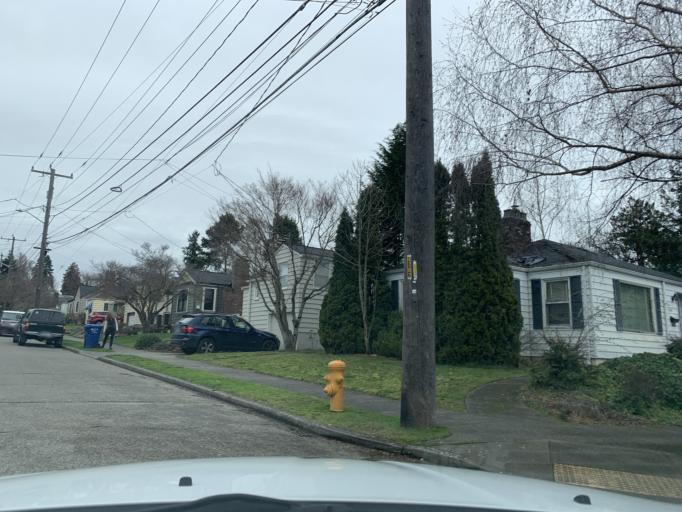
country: US
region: Washington
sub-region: King County
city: Seattle
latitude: 47.6626
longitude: -122.2892
